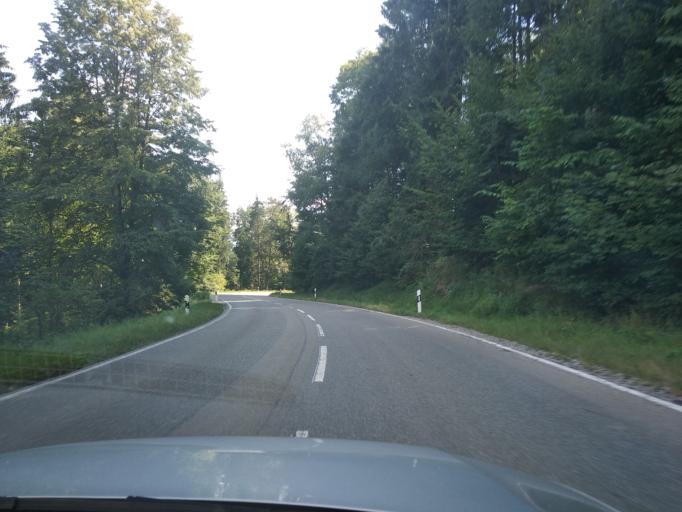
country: DE
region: Baden-Wuerttemberg
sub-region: Tuebingen Region
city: Leutkirch im Allgau
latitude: 47.8686
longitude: 10.0067
